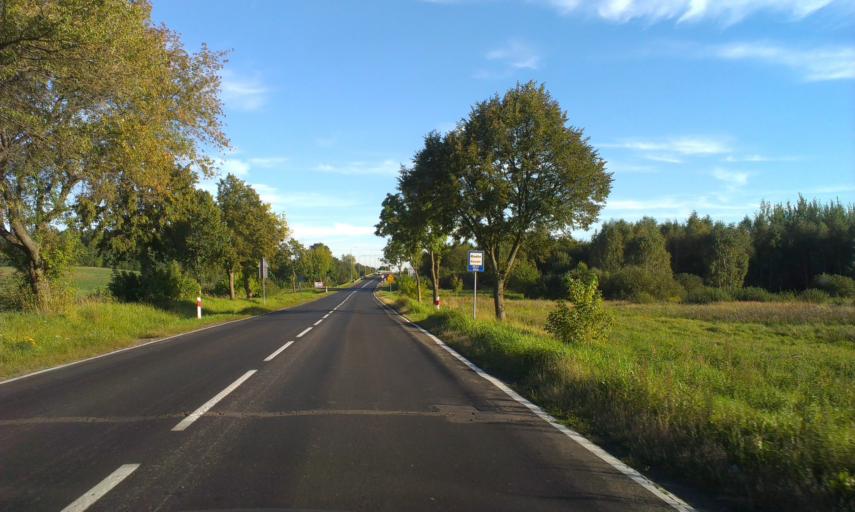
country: PL
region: West Pomeranian Voivodeship
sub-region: Powiat szczecinecki
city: Szczecinek
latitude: 53.7305
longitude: 16.6715
